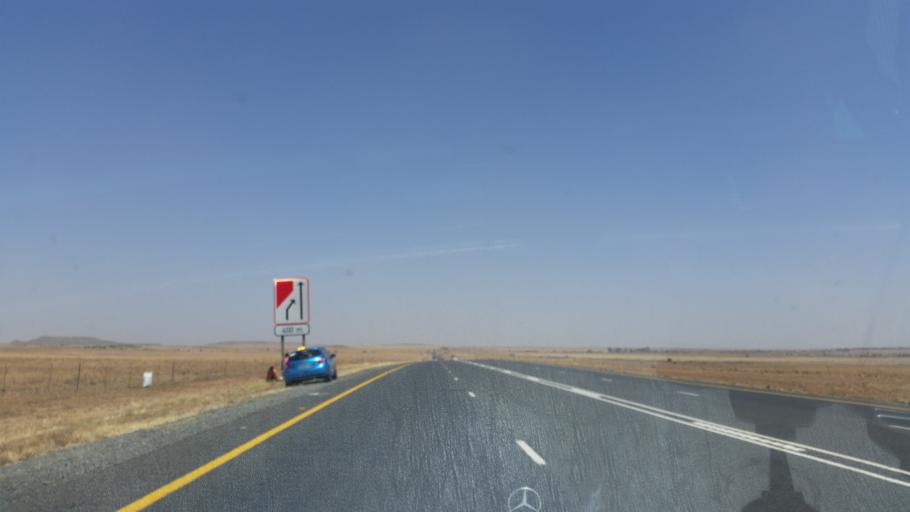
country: ZA
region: Orange Free State
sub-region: Lejweleputswa District Municipality
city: Brandfort
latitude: -28.7682
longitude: 26.7269
